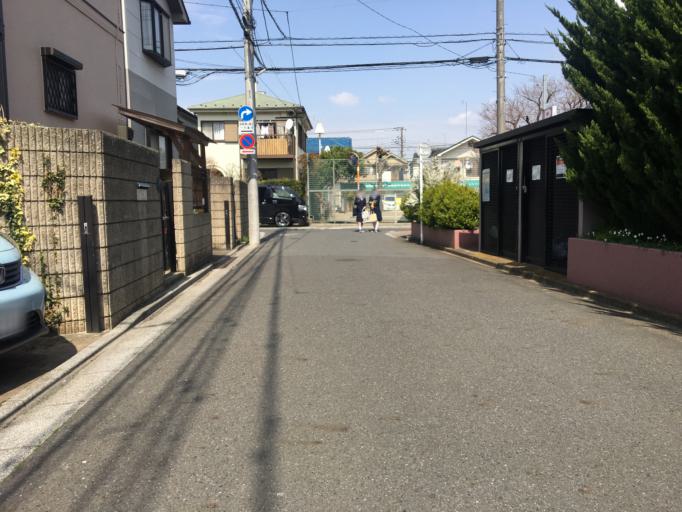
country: JP
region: Tokyo
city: Mitaka-shi
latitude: 35.6884
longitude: 139.5446
